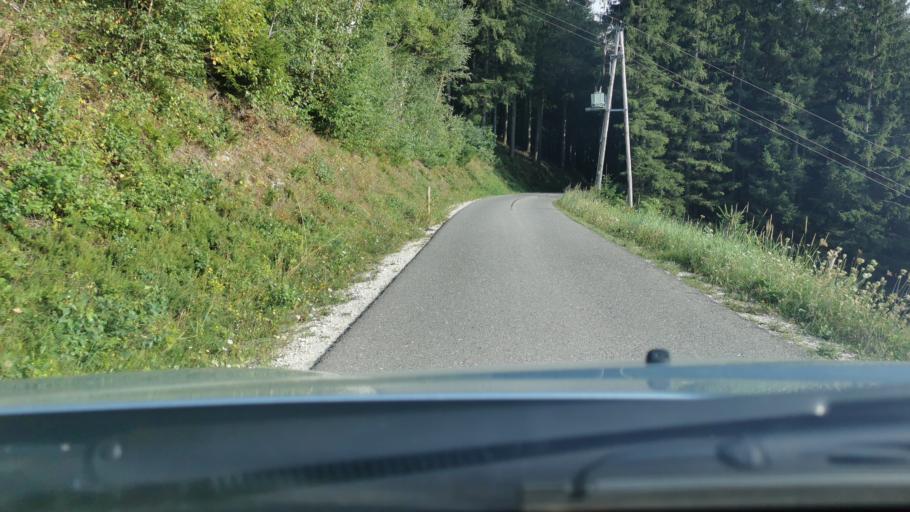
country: AT
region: Styria
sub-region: Politischer Bezirk Weiz
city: Fischbach
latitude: 47.3924
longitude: 15.6313
